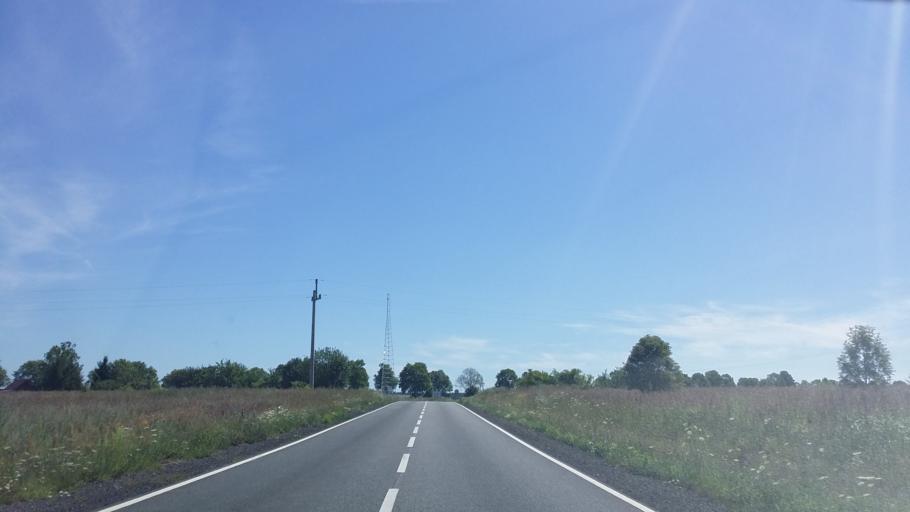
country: PL
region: West Pomeranian Voivodeship
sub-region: Powiat stargardzki
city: Insko
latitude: 53.4647
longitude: 15.5842
